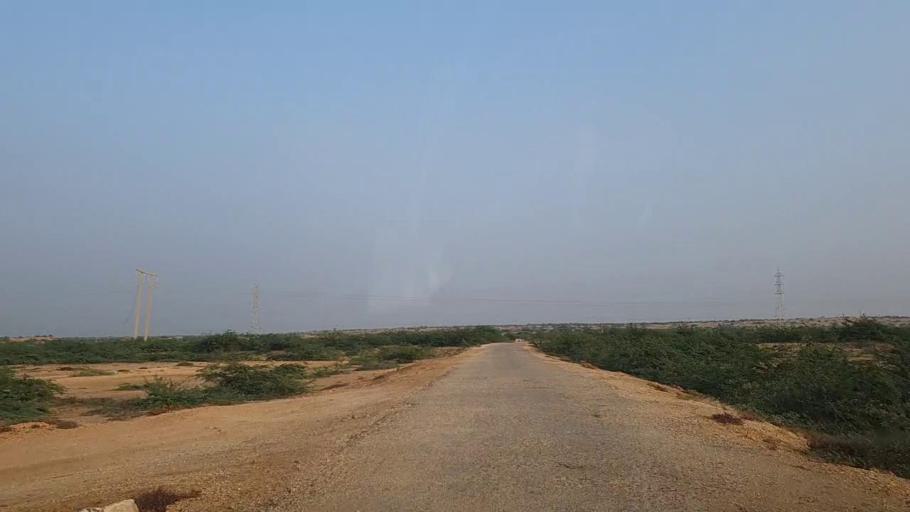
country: PK
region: Sindh
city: Thatta
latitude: 24.6897
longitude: 67.8489
